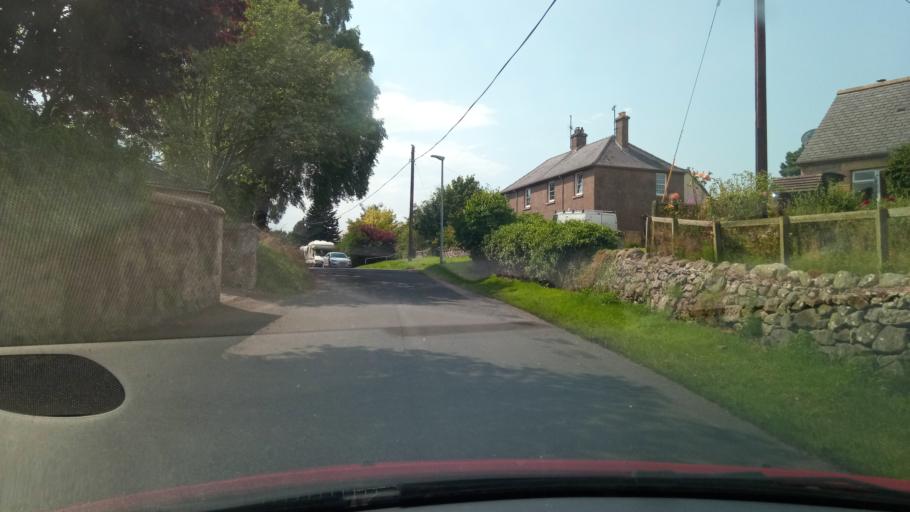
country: GB
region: Scotland
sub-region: The Scottish Borders
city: Kelso
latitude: 55.5692
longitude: -2.4765
